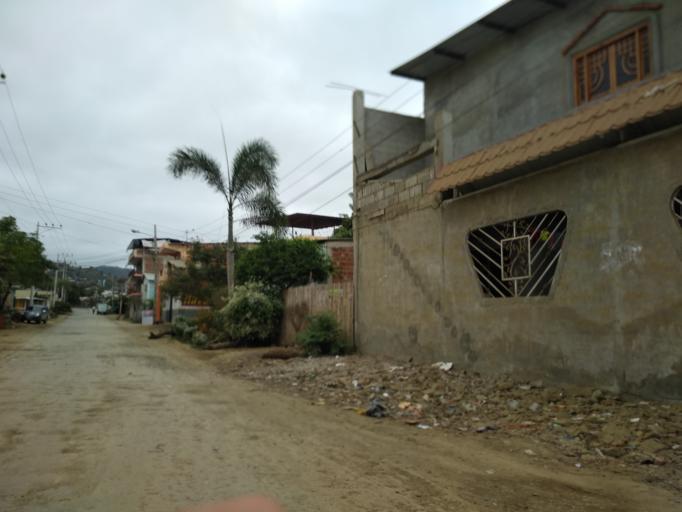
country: EC
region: Manabi
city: Jipijapa
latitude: -1.5527
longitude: -80.8092
